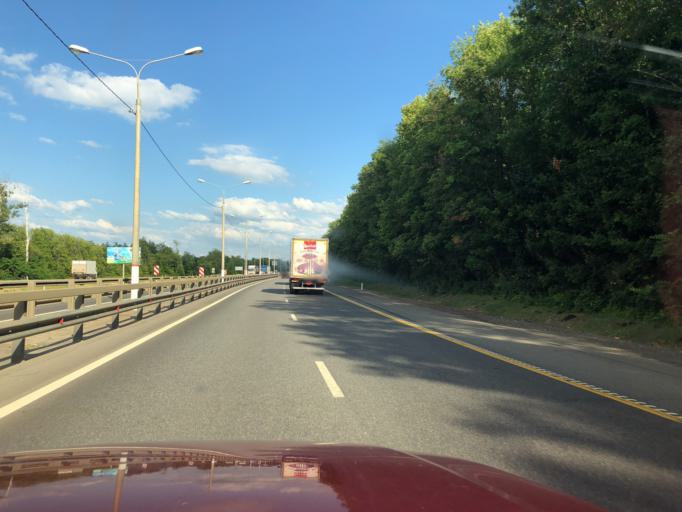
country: RU
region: Lipetsk
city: Zadonsk
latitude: 52.4410
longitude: 38.8002
